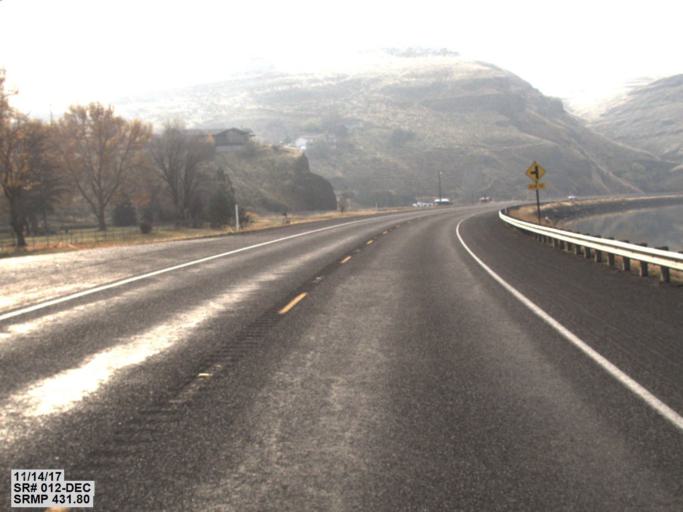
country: US
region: Washington
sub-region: Asotin County
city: West Clarkston-Highland
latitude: 46.4163
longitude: -117.0849
